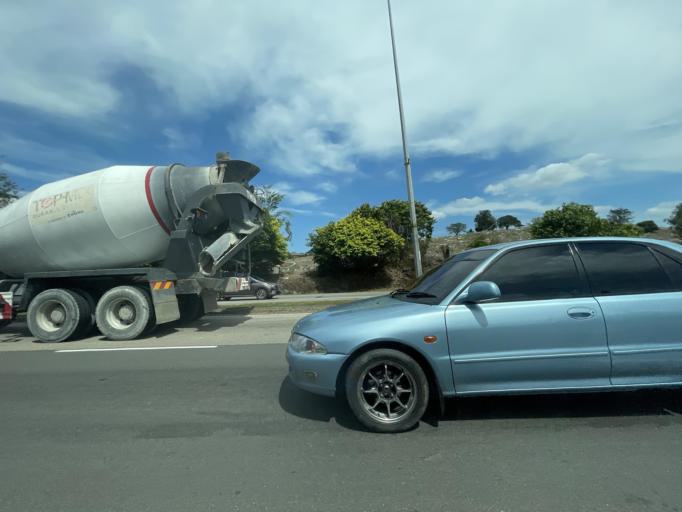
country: MY
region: Melaka
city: Batu Berendam
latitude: 2.2411
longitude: 102.2237
